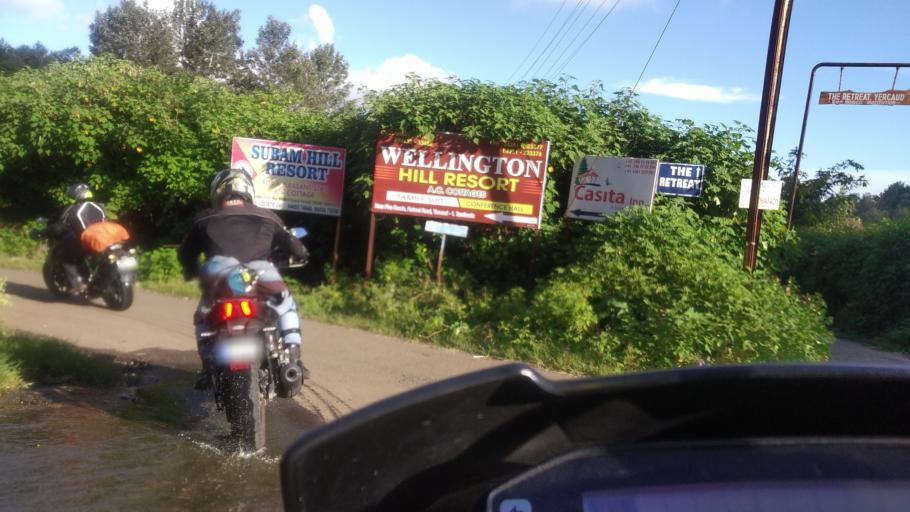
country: IN
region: Tamil Nadu
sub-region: Salem
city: Salem
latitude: 11.7696
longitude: 78.2105
